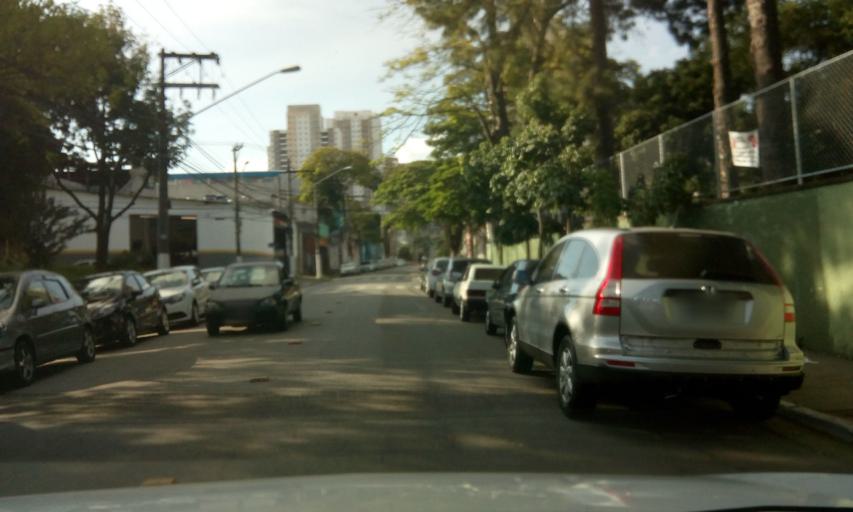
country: BR
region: Sao Paulo
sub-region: Sao Paulo
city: Sao Paulo
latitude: -23.5028
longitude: -46.6812
